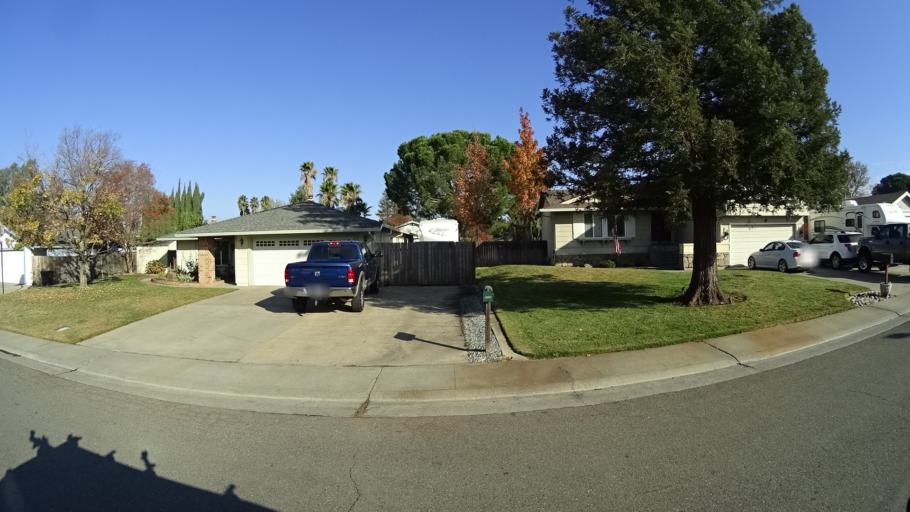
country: US
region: California
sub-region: Sacramento County
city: Citrus Heights
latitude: 38.7162
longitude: -121.2613
